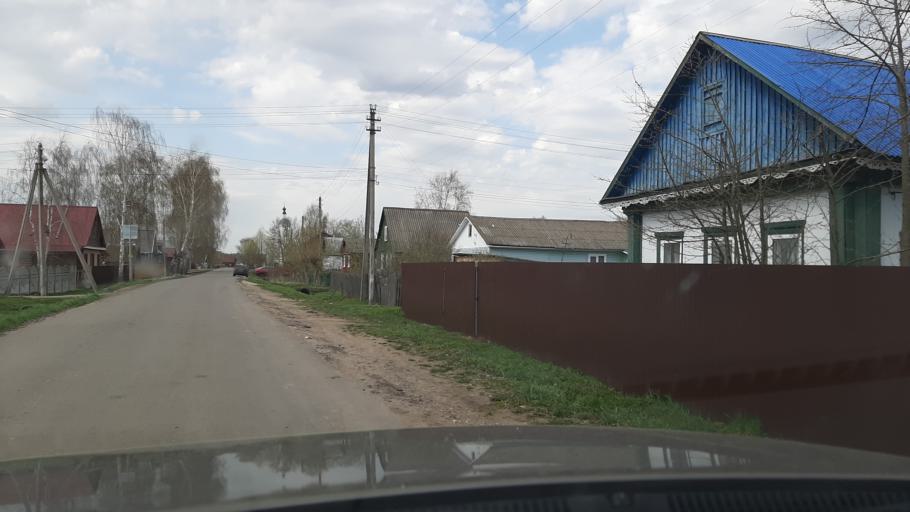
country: RU
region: Ivanovo
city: Privolzhsk
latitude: 57.3301
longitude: 41.2344
